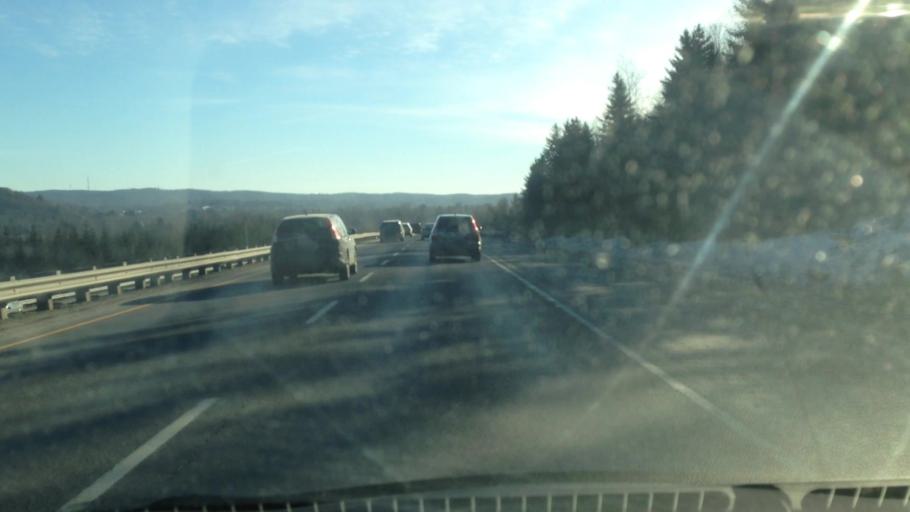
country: CA
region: Quebec
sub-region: Laurentides
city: Prevost
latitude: 45.8792
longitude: -74.0970
